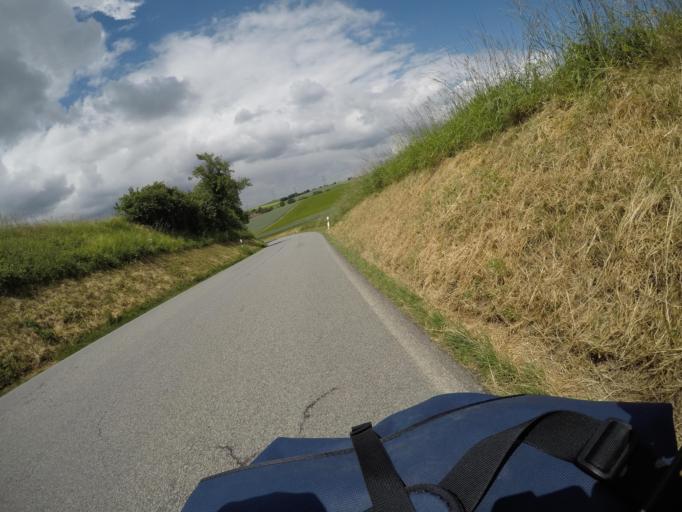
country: DE
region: Baden-Wuerttemberg
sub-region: Karlsruhe Region
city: Sinsheim
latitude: 49.1947
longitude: 8.8722
